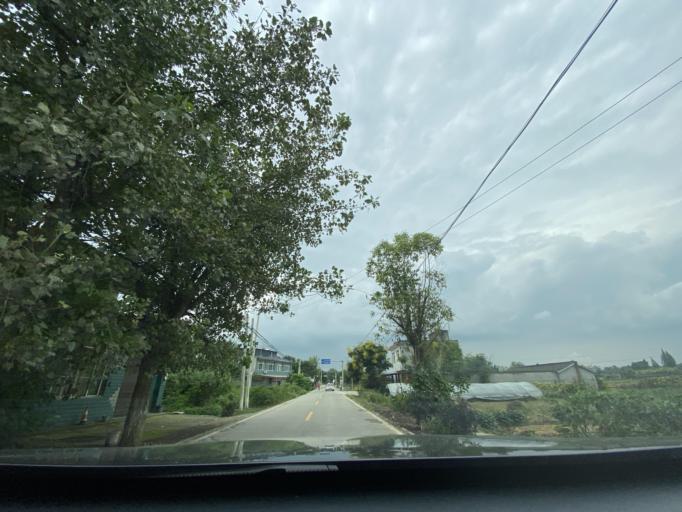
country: CN
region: Sichuan
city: Wujin
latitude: 30.3754
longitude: 103.9684
